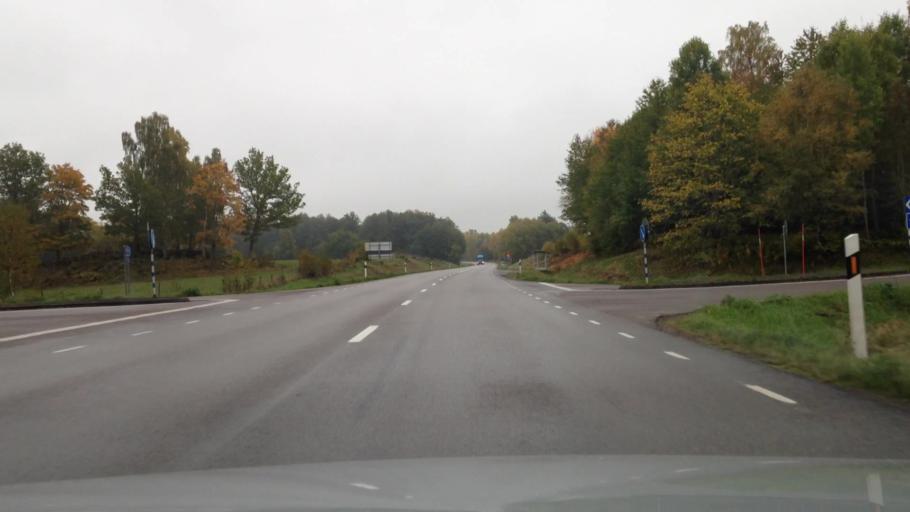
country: SE
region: Vaestra Goetaland
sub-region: Falkopings Kommun
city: Falkoeping
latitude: 58.2498
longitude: 13.5120
